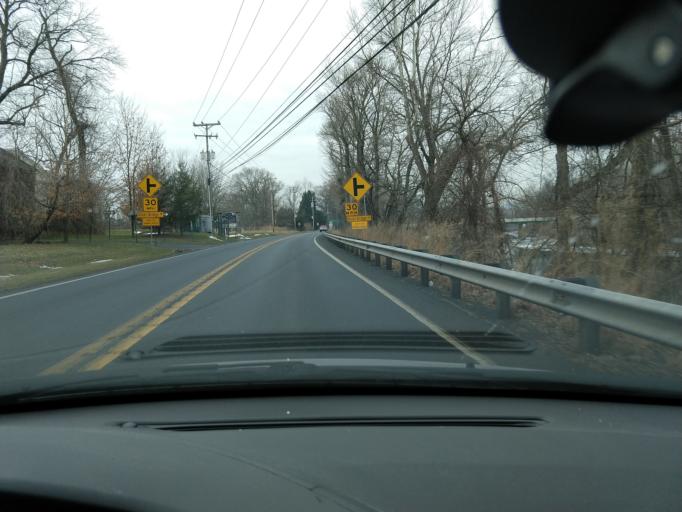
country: US
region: Pennsylvania
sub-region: Berks County
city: Amity Gardens
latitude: 40.2485
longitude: -75.7228
